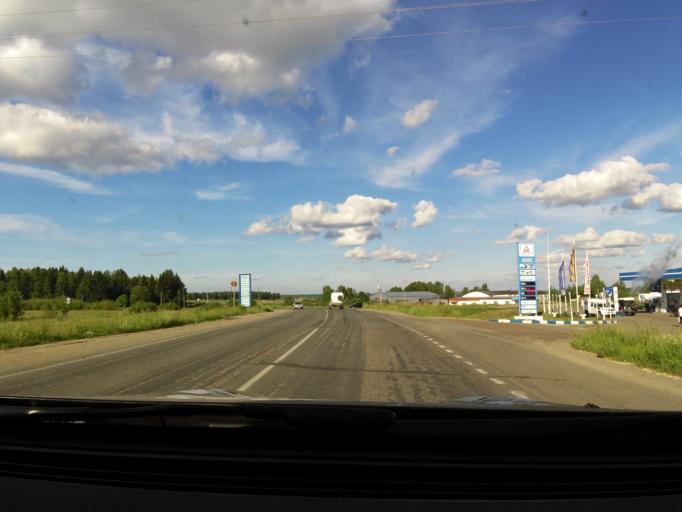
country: RU
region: Kirov
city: Omutninsk
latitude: 58.6894
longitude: 52.1880
